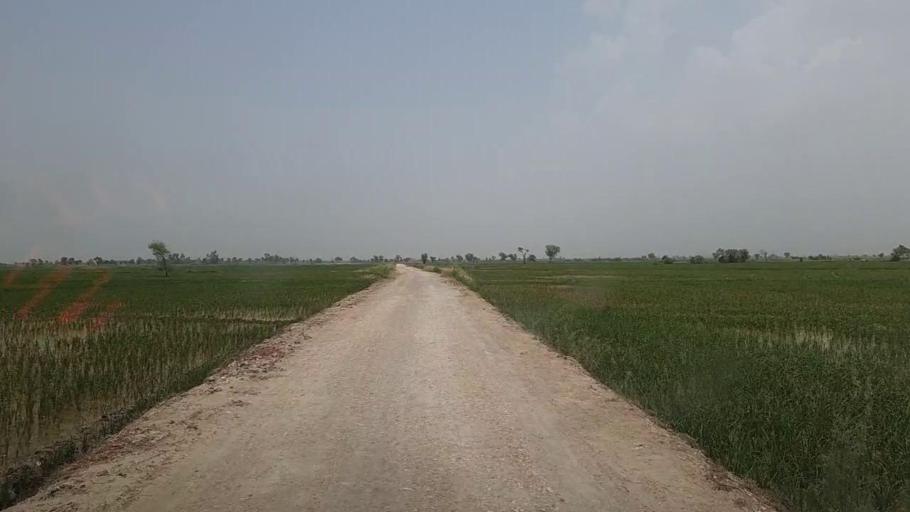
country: PK
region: Sindh
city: Sita Road
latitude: 27.0729
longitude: 67.8673
